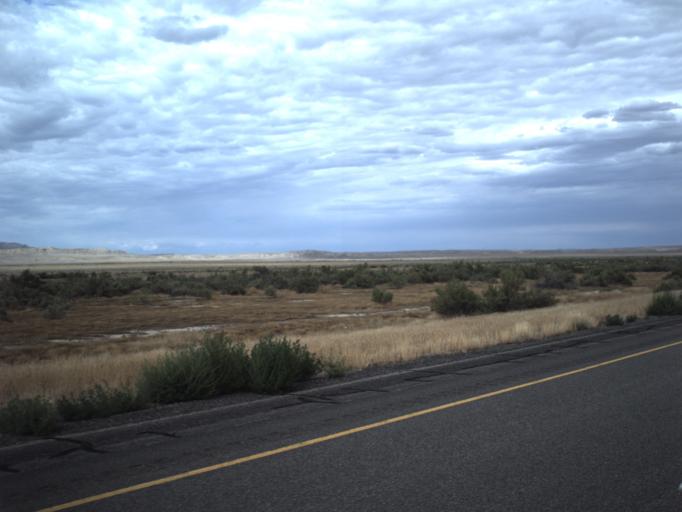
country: US
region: Utah
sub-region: Grand County
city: Moab
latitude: 38.9418
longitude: -109.5971
